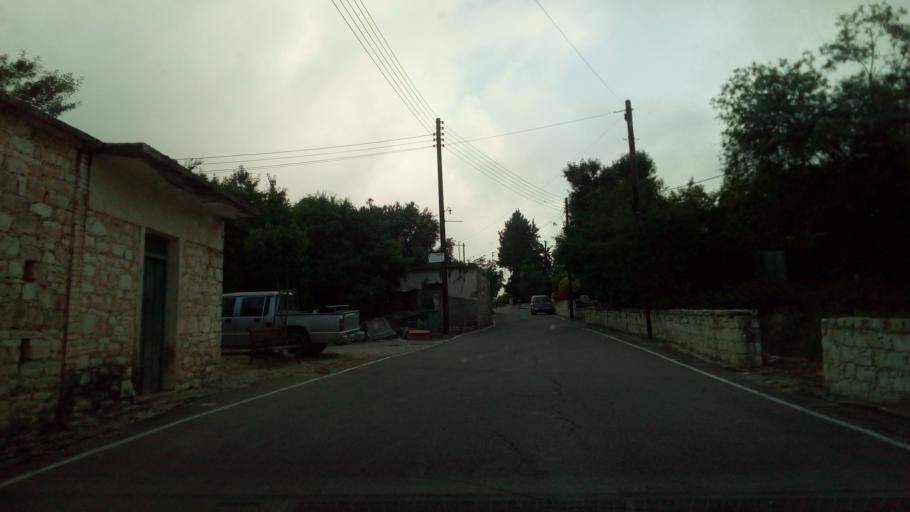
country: CY
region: Limassol
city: Pachna
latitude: 34.8388
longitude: 32.6896
